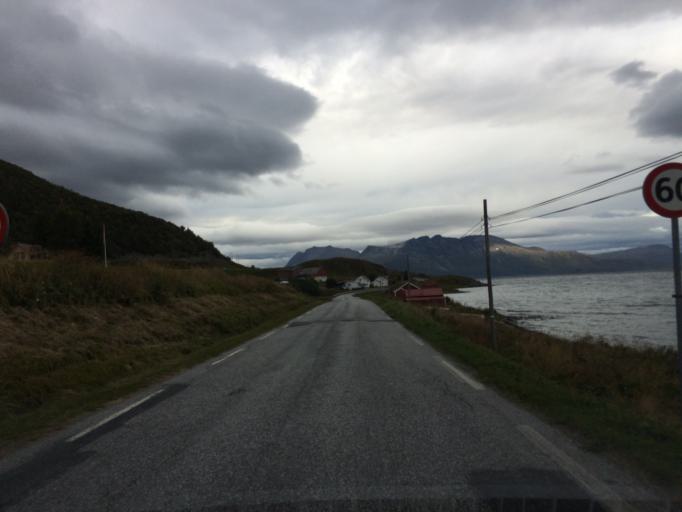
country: NO
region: Troms
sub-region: Lenvik
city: Finnsnes
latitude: 69.5207
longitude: 18.1985
